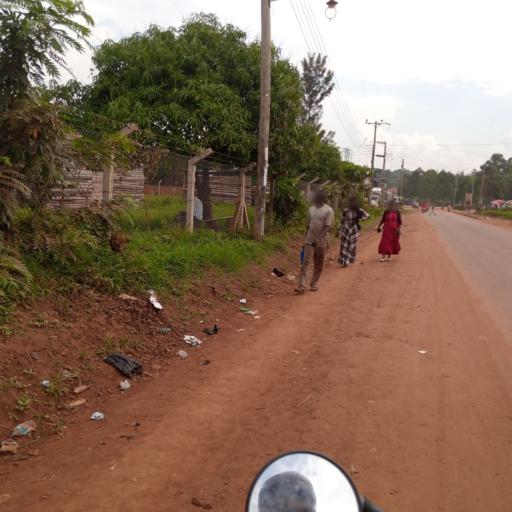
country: UG
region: Eastern Region
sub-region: Mbale District
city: Mbale
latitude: 1.0854
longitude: 34.1799
